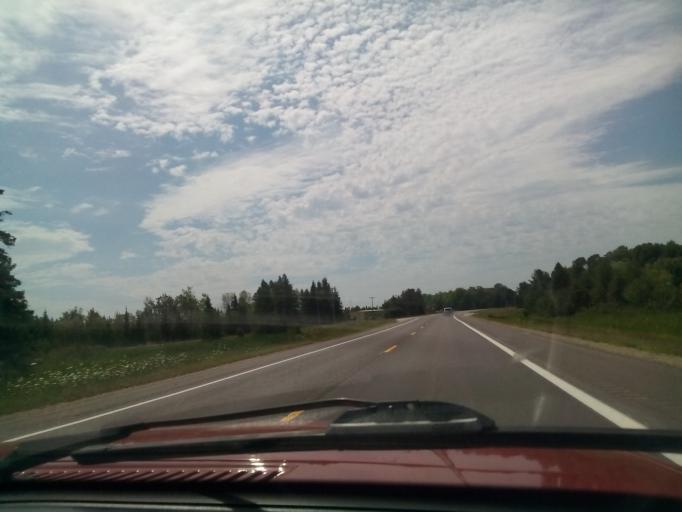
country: US
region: Michigan
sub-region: Schoolcraft County
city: Manistique
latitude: 45.9990
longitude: -86.0038
